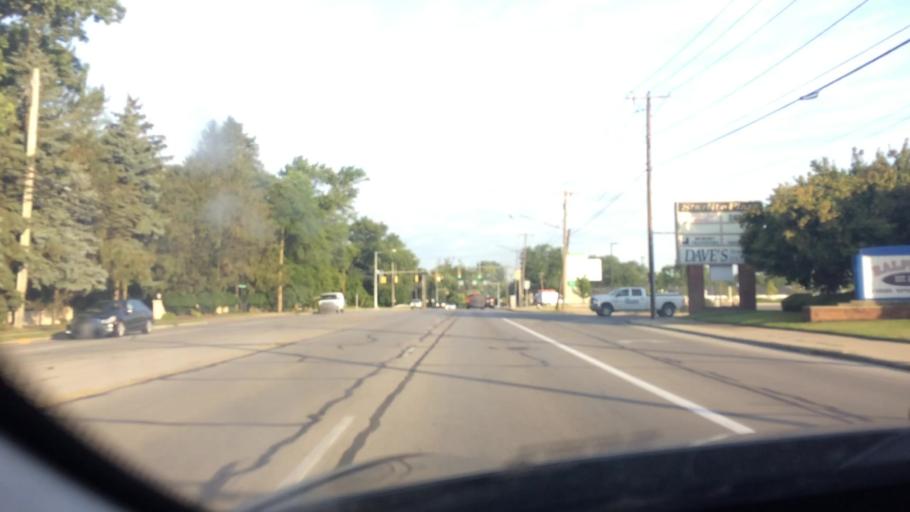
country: US
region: Ohio
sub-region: Lucas County
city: Sylvania
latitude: 41.7094
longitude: -83.6755
